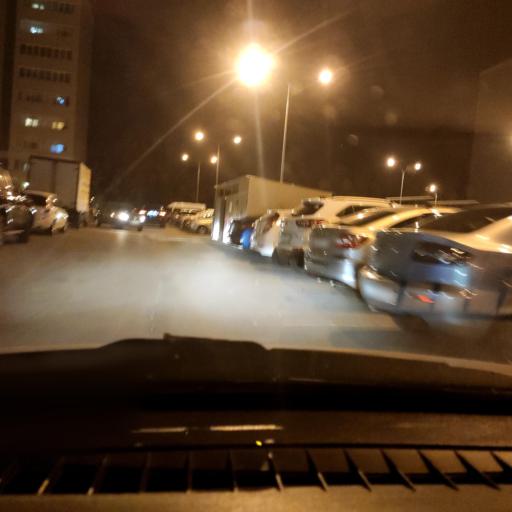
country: RU
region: Samara
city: Tol'yatti
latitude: 53.5473
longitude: 49.3121
